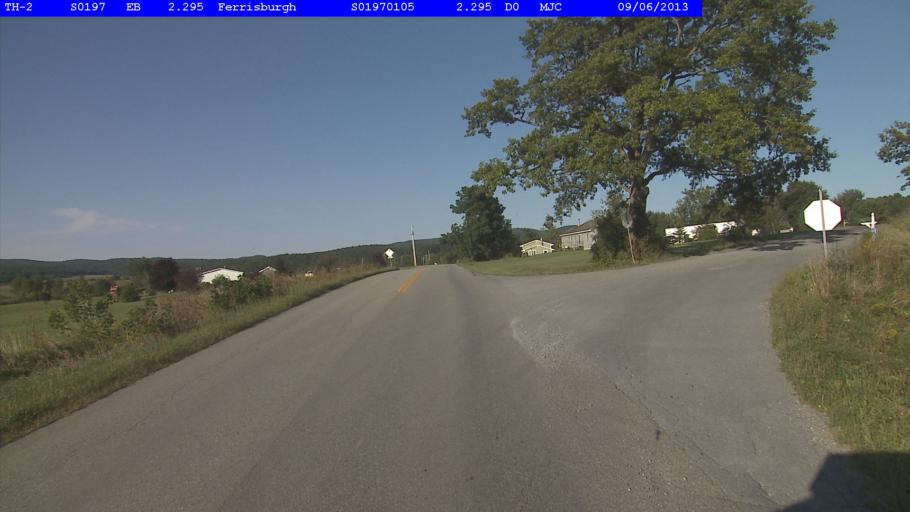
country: US
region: Vermont
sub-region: Addison County
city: Vergennes
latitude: 44.1771
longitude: -73.1945
